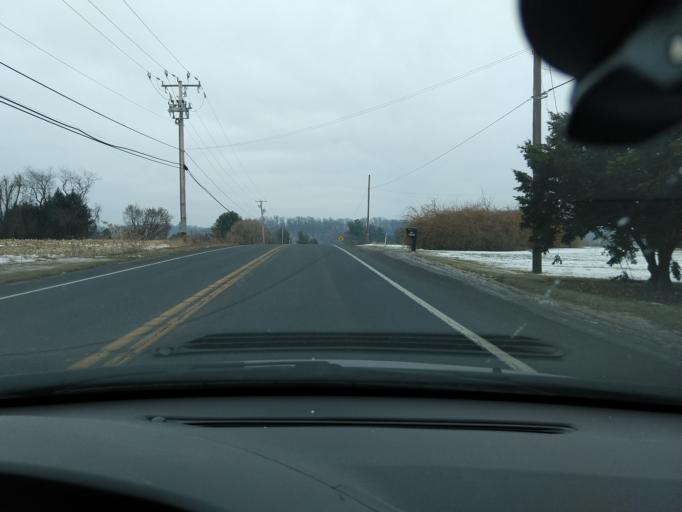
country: US
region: Pennsylvania
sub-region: Lehigh County
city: Macungie
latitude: 40.4866
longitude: -75.5235
